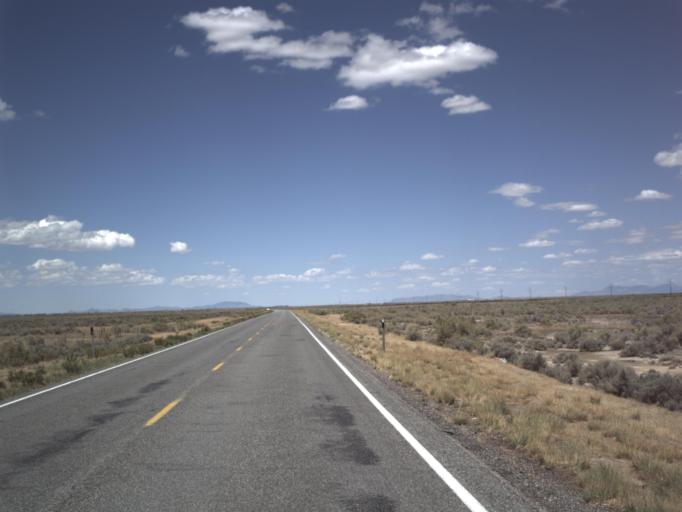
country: US
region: Utah
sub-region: Millard County
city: Delta
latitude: 39.2507
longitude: -112.4395
